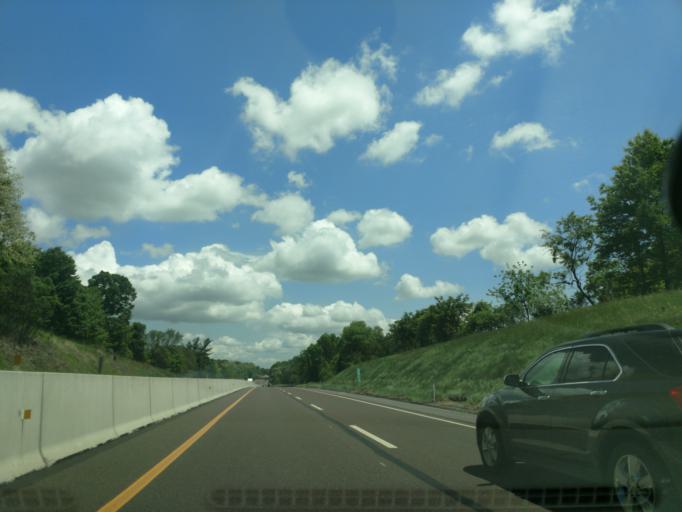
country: US
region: Pennsylvania
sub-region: Lancaster County
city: Schoeneck
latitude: 40.2450
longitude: -76.1705
